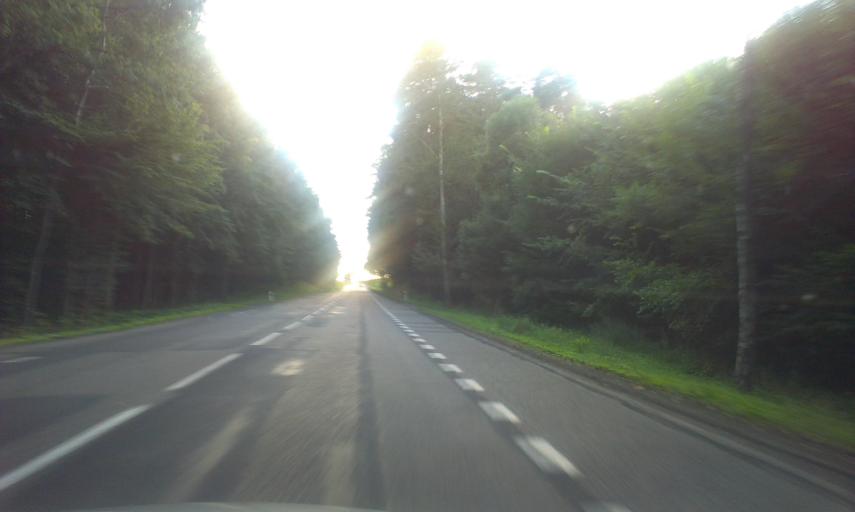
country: PL
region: West Pomeranian Voivodeship
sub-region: Powiat koszalinski
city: Sianow
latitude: 54.2551
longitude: 16.3709
